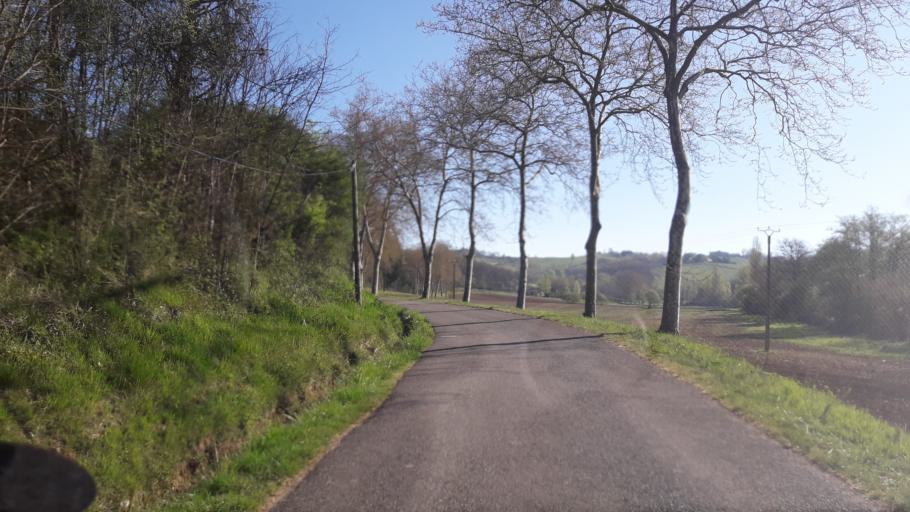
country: FR
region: Midi-Pyrenees
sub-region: Departement de la Haute-Garonne
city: Montesquieu-Volvestre
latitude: 43.1962
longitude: 1.2583
